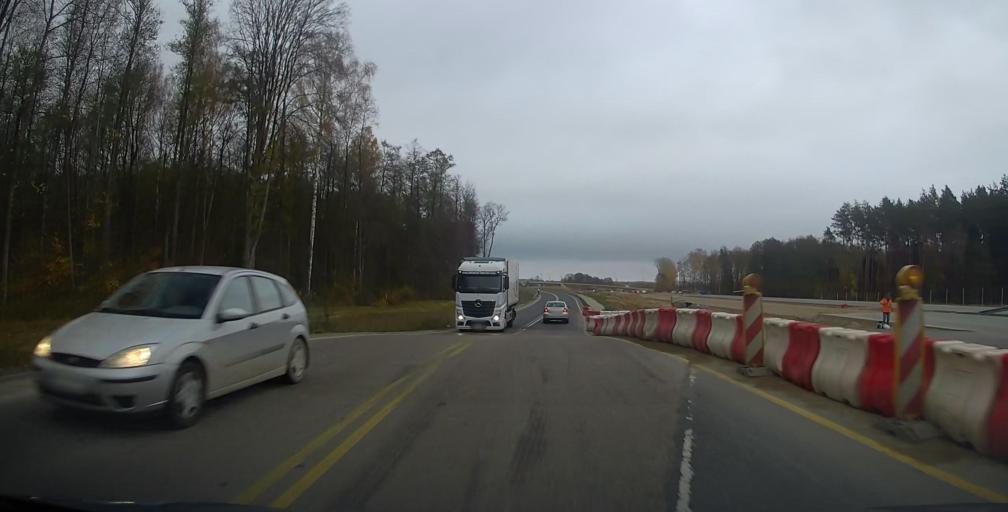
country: PL
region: Warmian-Masurian Voivodeship
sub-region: Powiat elcki
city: Elk
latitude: 53.8443
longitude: 22.4511
